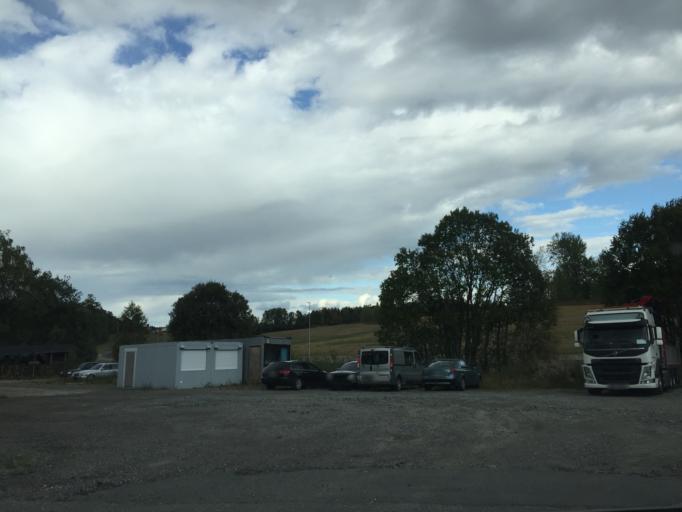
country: NO
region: Ostfold
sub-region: Spydeberg
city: Spydeberg
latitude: 59.5891
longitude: 11.1133
